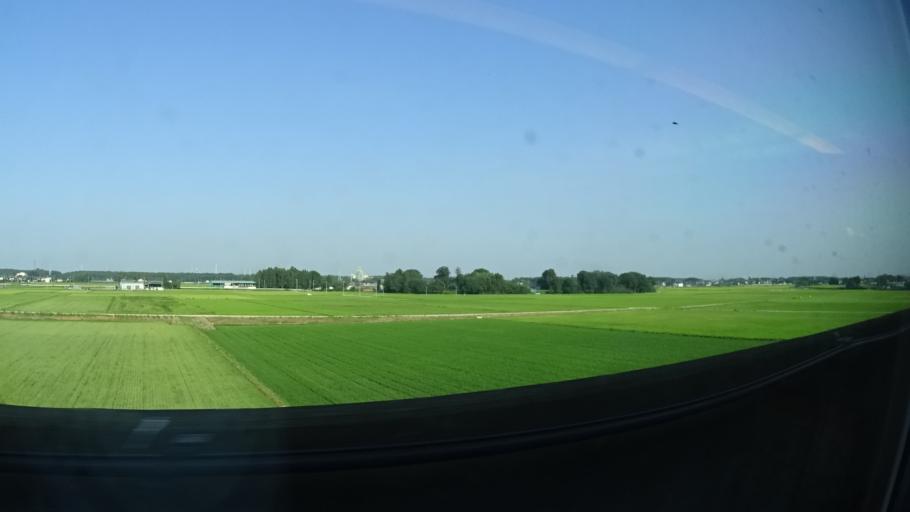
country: JP
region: Tochigi
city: Utsunomiya-shi
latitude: 36.6287
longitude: 139.9093
